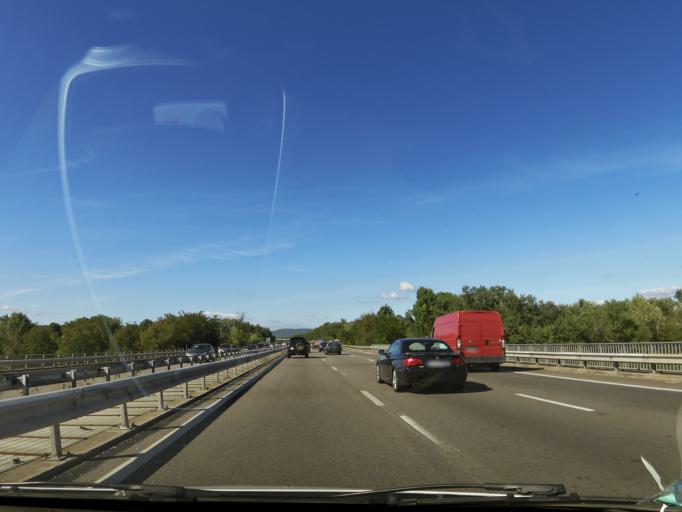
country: FR
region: Rhone-Alpes
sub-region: Departement de la Drome
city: Montboucher-sur-Jabron
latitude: 44.5450
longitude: 4.8079
